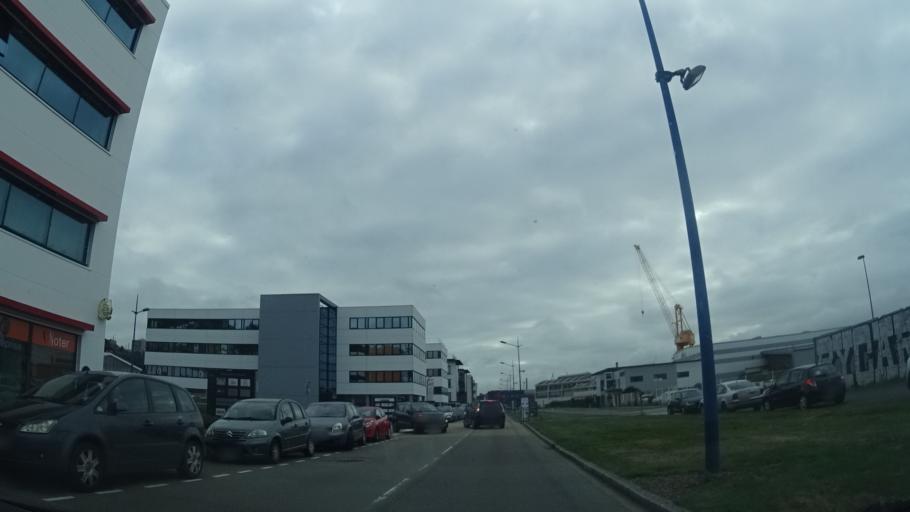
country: FR
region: Brittany
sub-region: Departement du Finistere
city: Brest
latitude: 48.3849
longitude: -4.4798
